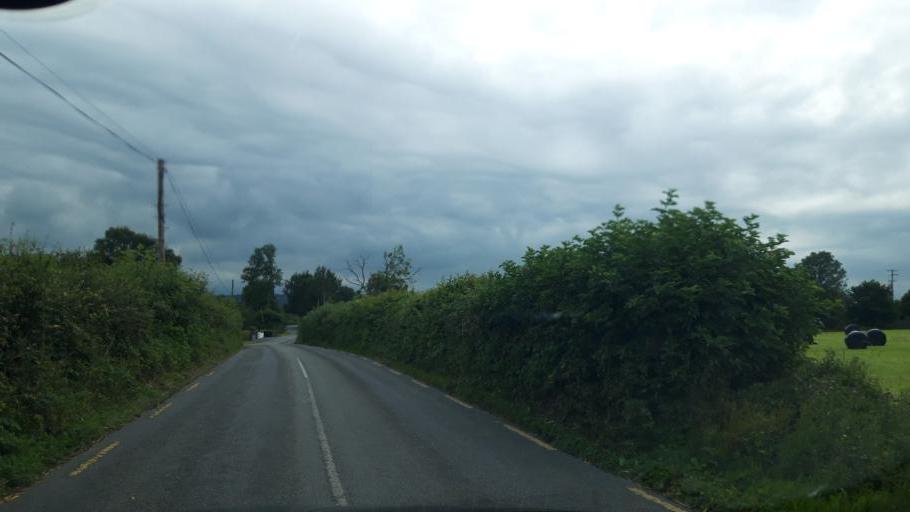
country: IE
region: Leinster
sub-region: Kilkenny
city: Ballyragget
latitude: 52.7470
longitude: -7.3936
